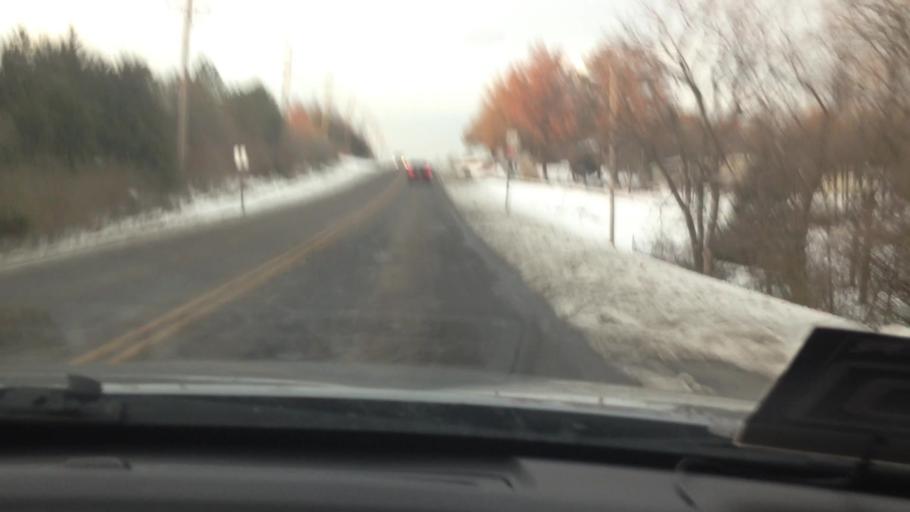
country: US
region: Kansas
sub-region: Leavenworth County
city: Lansing
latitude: 39.2412
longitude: -94.9190
